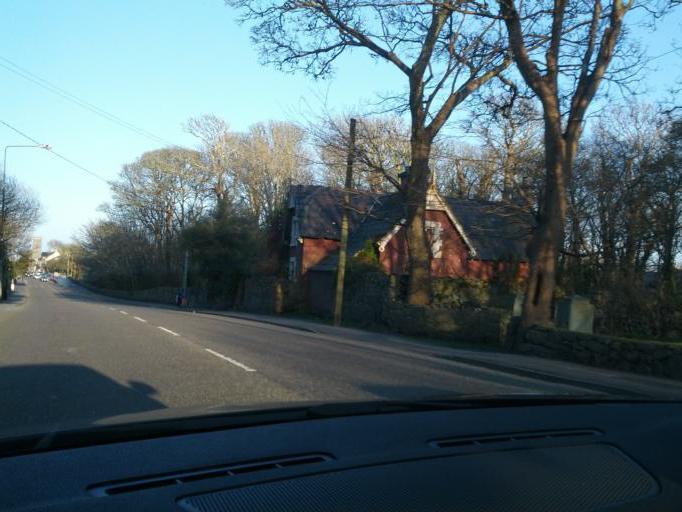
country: IE
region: Connaught
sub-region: County Galway
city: Moycullen
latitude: 53.2441
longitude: -9.3107
